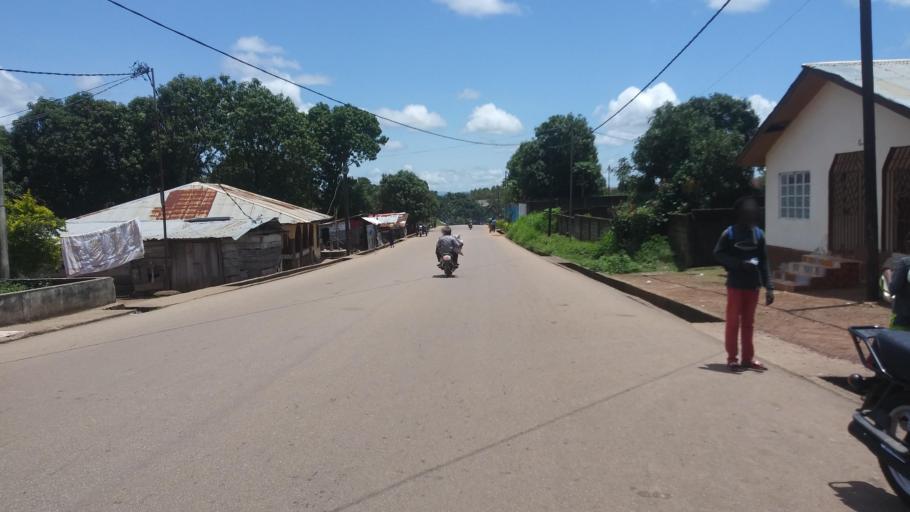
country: SL
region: Northern Province
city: Makeni
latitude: 8.8793
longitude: -12.0320
